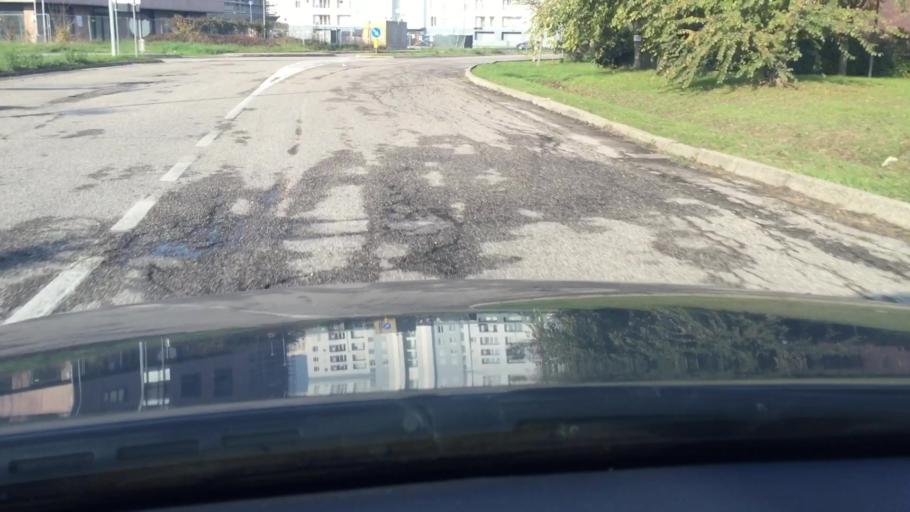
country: IT
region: Emilia-Romagna
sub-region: Provincia di Ferrara
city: Ferrara
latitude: 44.8188
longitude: 11.5966
